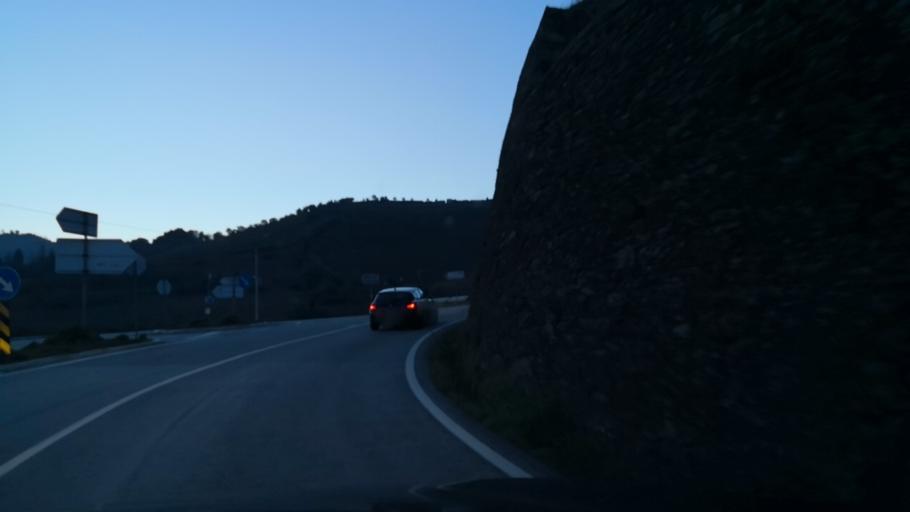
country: PT
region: Vila Real
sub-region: Mesao Frio
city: Mesao Frio
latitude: 41.1587
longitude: -7.8799
